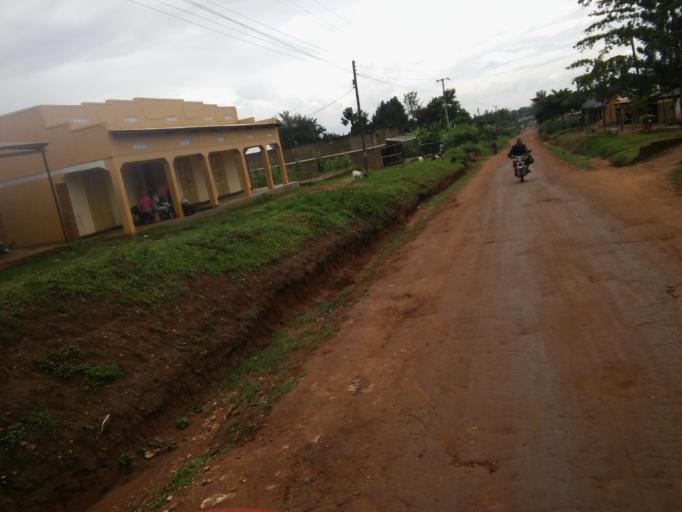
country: UG
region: Eastern Region
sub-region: Mbale District
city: Mbale
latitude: 1.0391
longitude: 34.1833
